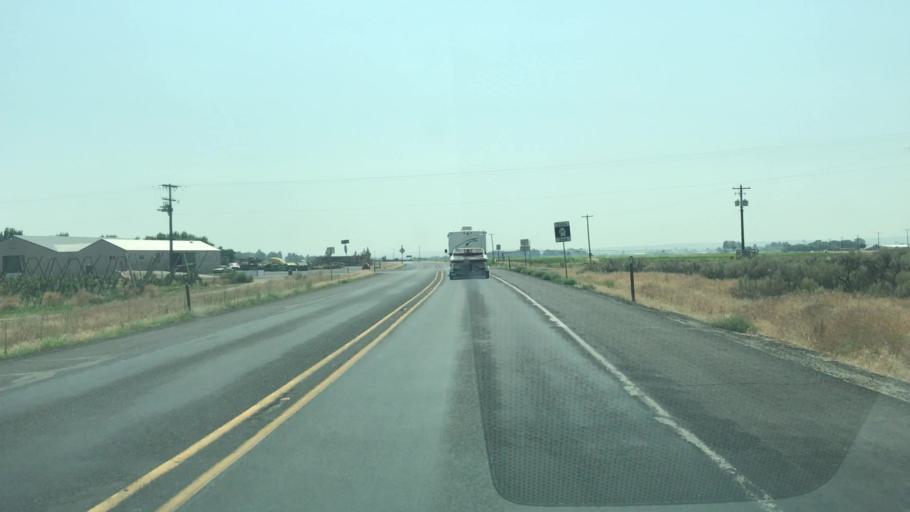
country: US
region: Washington
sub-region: Grant County
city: Quincy
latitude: 47.1185
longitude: -119.8527
